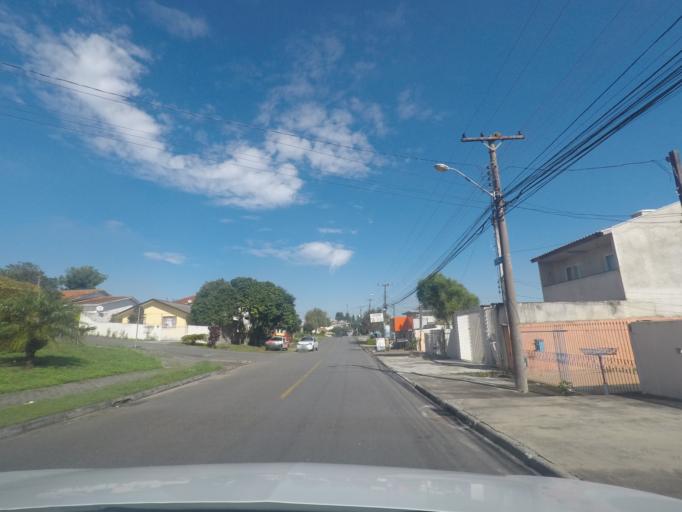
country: BR
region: Parana
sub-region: Sao Jose Dos Pinhais
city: Sao Jose dos Pinhais
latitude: -25.5069
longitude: -49.2584
